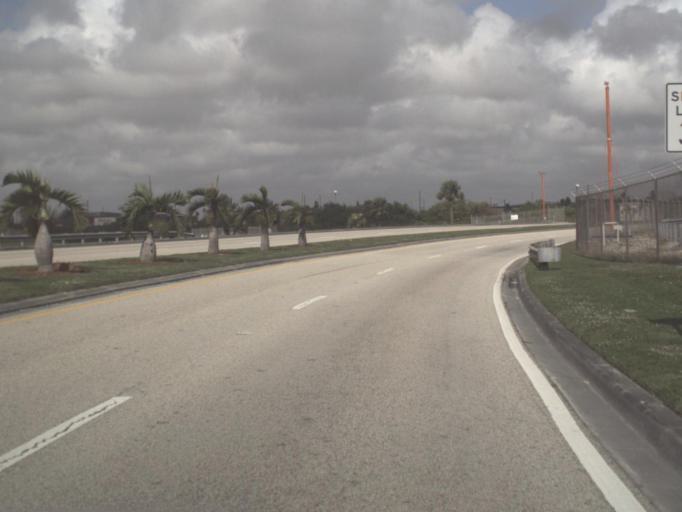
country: US
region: Florida
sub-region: Miami-Dade County
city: Virginia Gardens
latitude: 25.8001
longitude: -80.3065
